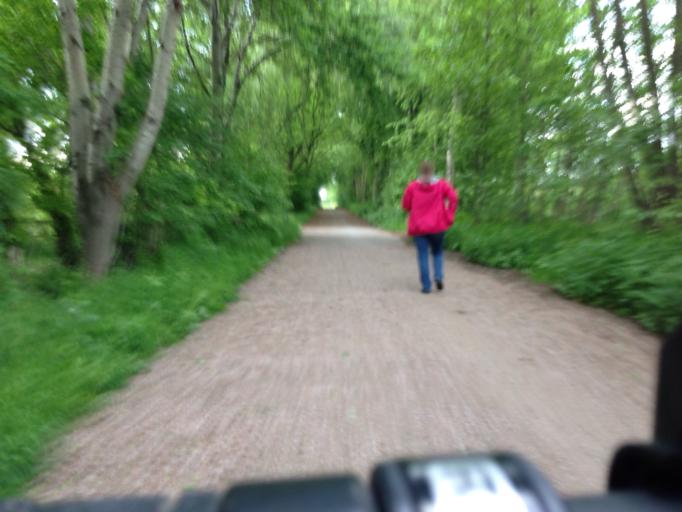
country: DE
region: Schleswig-Holstein
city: Barsbuettel
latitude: 53.5789
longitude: 10.1912
